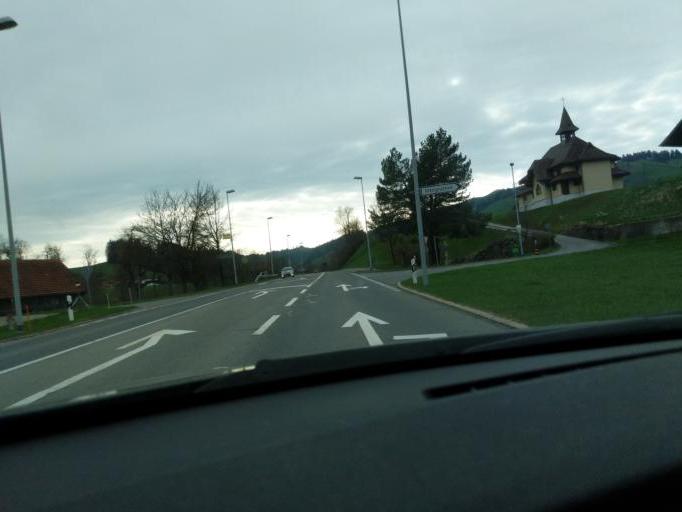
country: CH
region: Lucerne
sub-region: Entlebuch District
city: Escholzmatt
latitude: 46.9293
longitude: 7.9688
